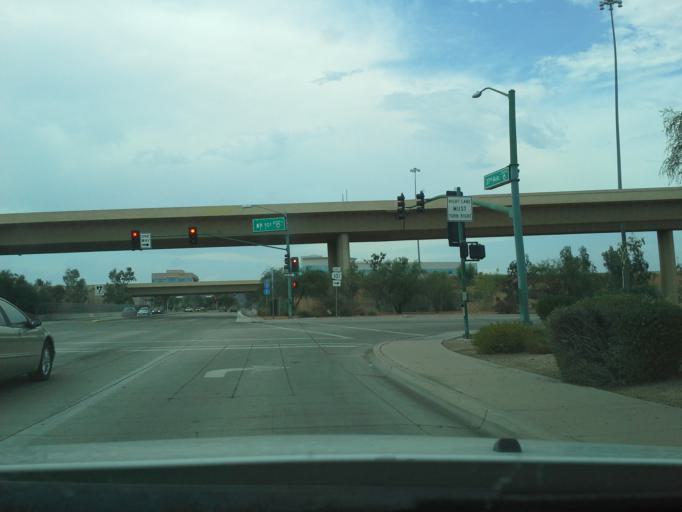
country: US
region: Arizona
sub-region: Maricopa County
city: Glendale
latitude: 33.6675
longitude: -112.1171
